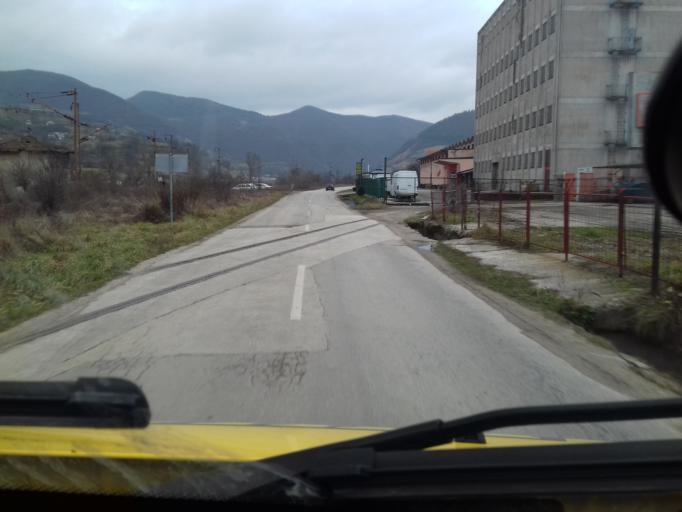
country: BA
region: Federation of Bosnia and Herzegovina
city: Zenica
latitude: 44.1683
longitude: 17.9681
